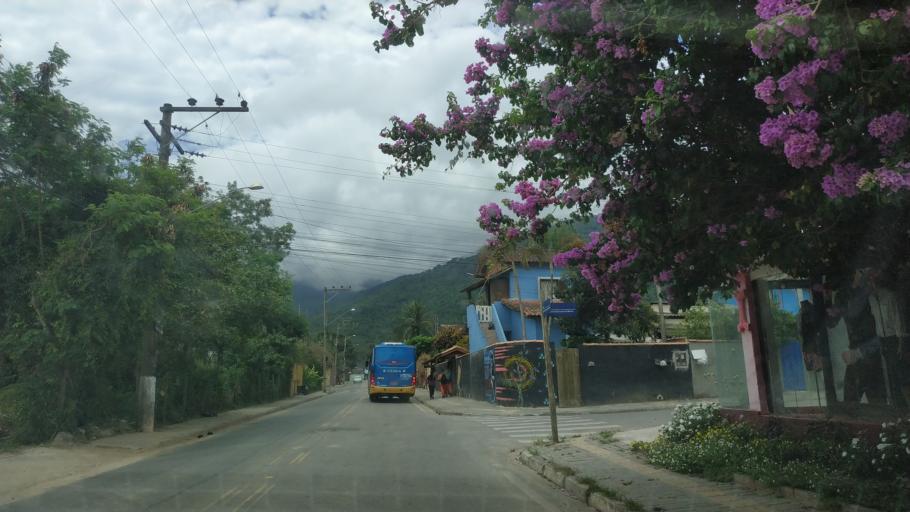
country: BR
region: Sao Paulo
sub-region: Ilhabela
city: Ilhabela
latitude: -23.8224
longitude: -45.3599
